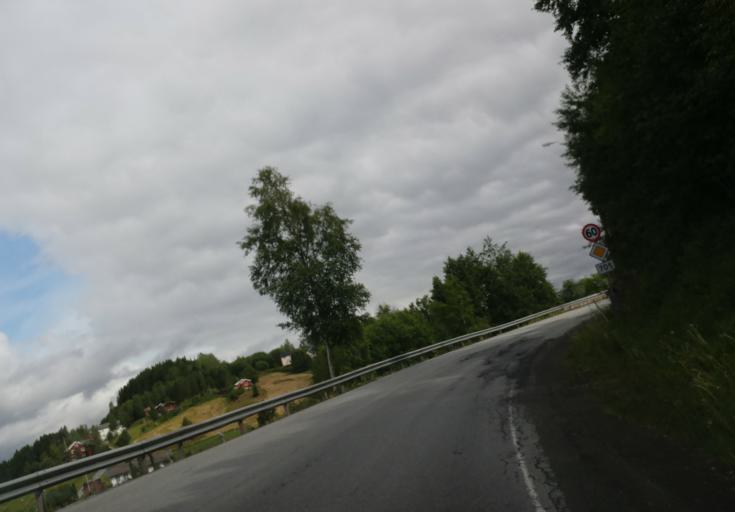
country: NO
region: Sor-Trondelag
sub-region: Selbu
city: Mebonden
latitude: 63.2405
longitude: 11.0500
